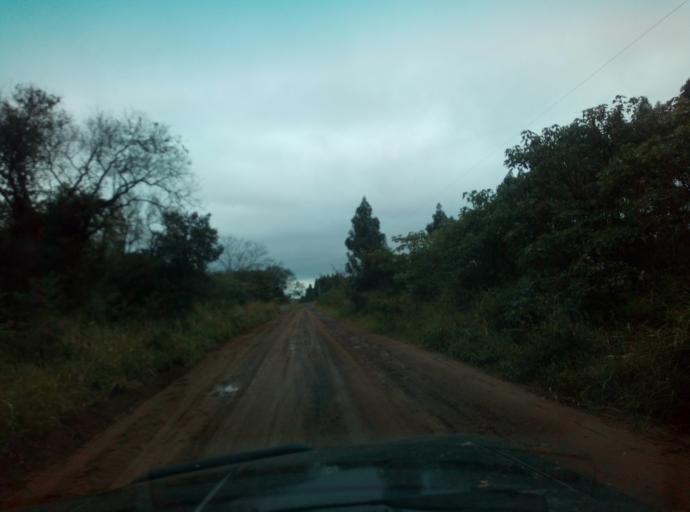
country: PY
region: Caaguazu
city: Carayao
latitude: -25.1902
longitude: -56.3886
